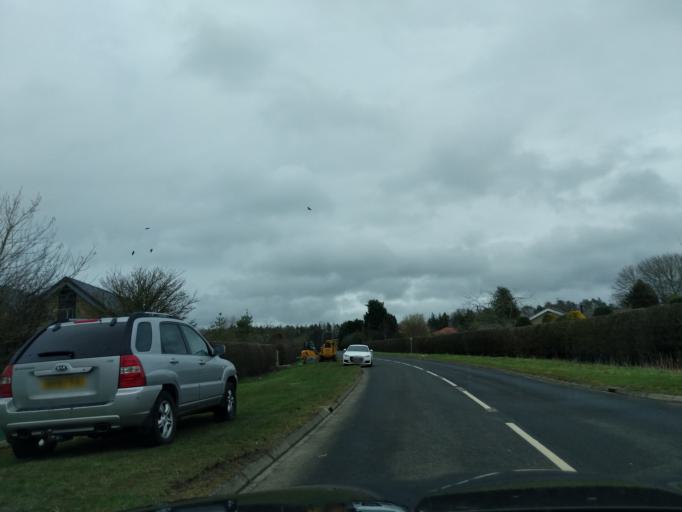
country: GB
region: England
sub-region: Northumberland
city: Morpeth
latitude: 55.1806
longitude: -1.7201
